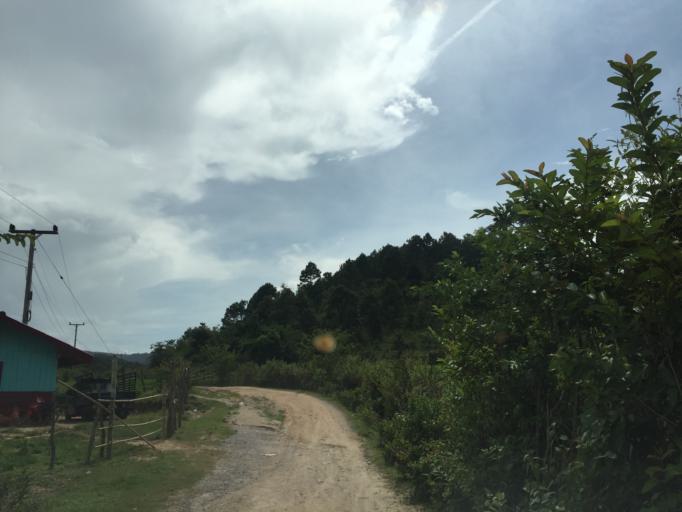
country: LA
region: Xiangkhoang
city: Muang Phonsavan
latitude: 19.3397
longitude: 103.5316
